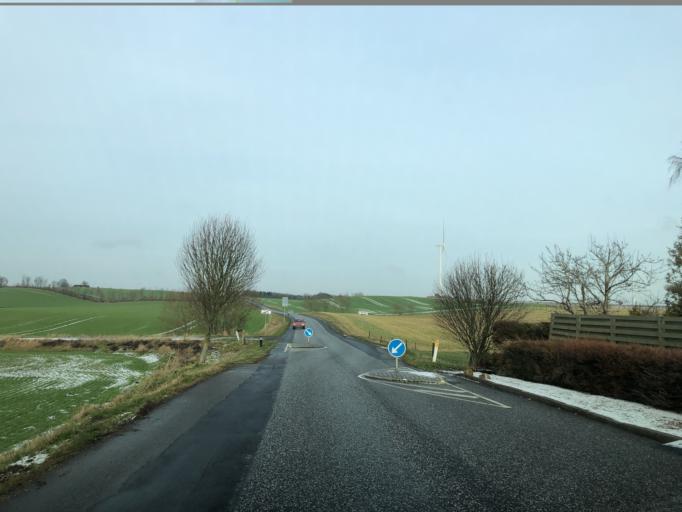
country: DK
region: Central Jutland
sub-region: Hedensted Kommune
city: Torring
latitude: 55.8136
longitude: 9.4724
